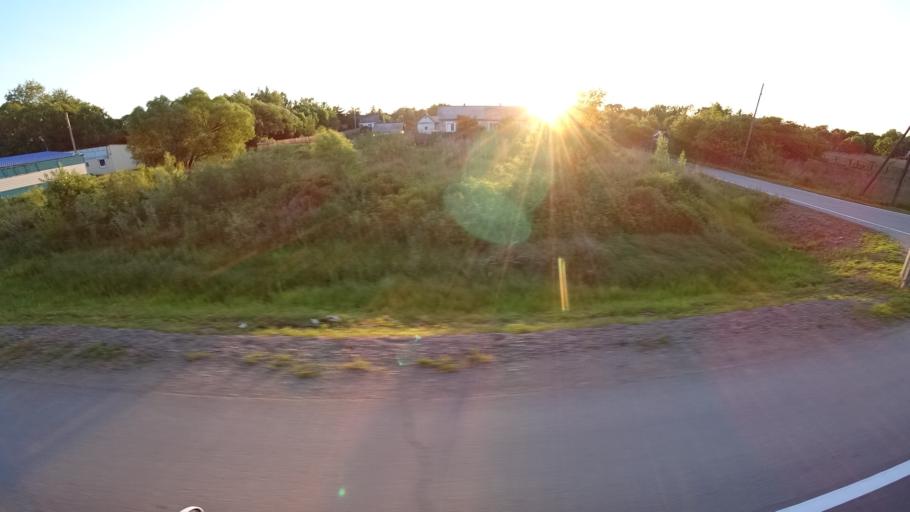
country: RU
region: Khabarovsk Krai
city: Khor
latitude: 47.8545
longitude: 134.9616
